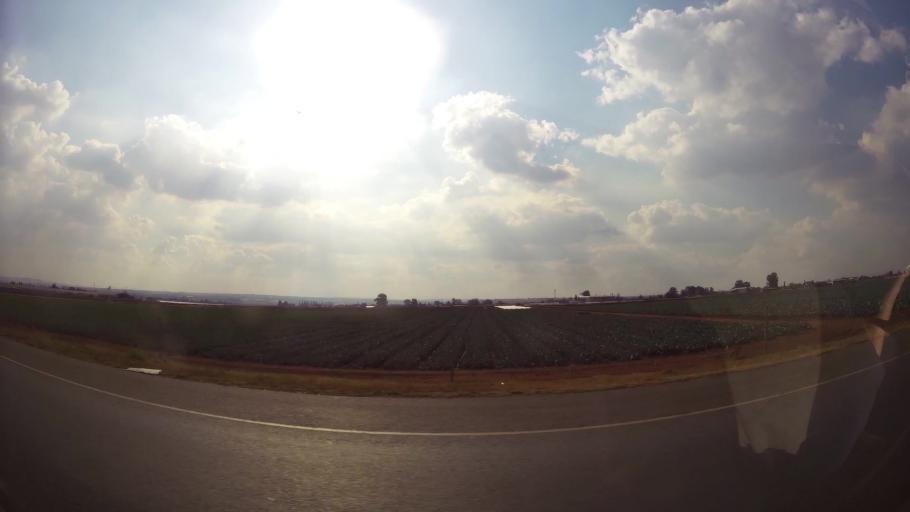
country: ZA
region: Gauteng
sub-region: Ekurhuleni Metropolitan Municipality
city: Germiston
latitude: -26.2910
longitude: 28.2251
